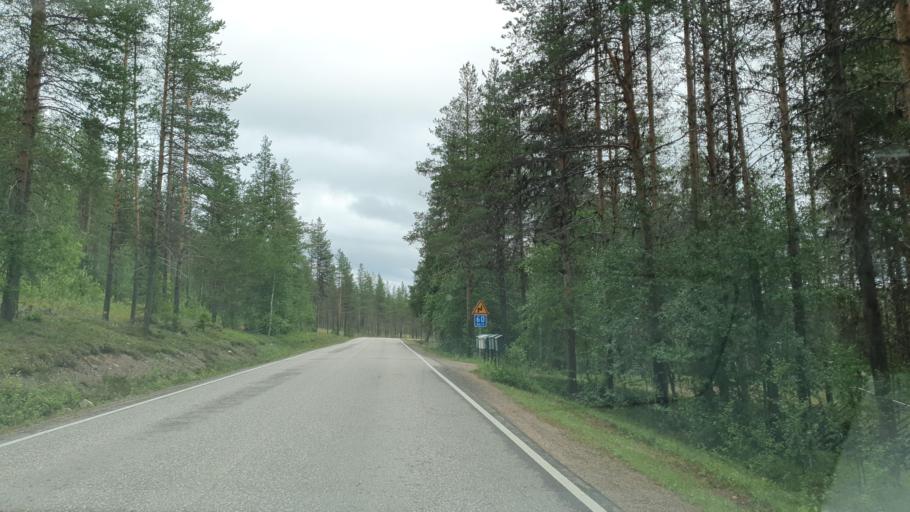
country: FI
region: Lapland
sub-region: Tunturi-Lappi
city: Kolari
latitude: 67.5757
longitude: 24.0620
